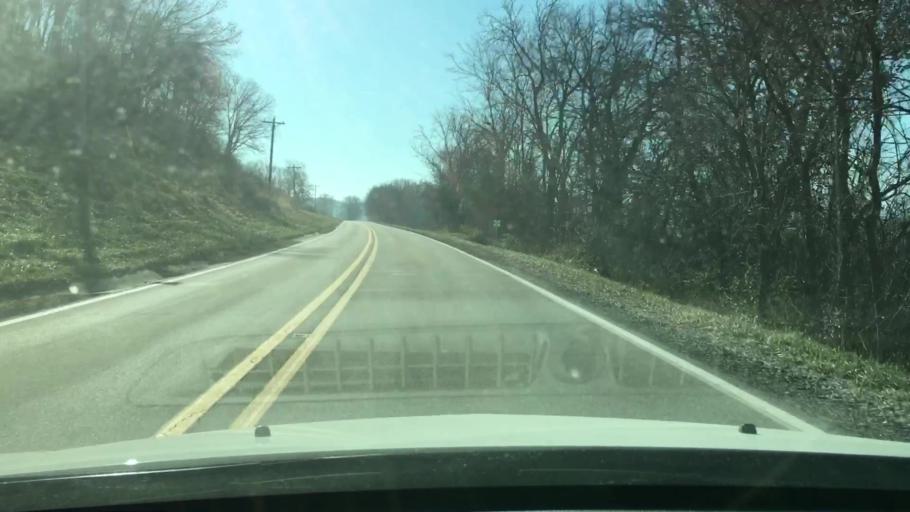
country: US
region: Illinois
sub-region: Morgan County
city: Meredosia
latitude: 39.7211
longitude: -90.5685
